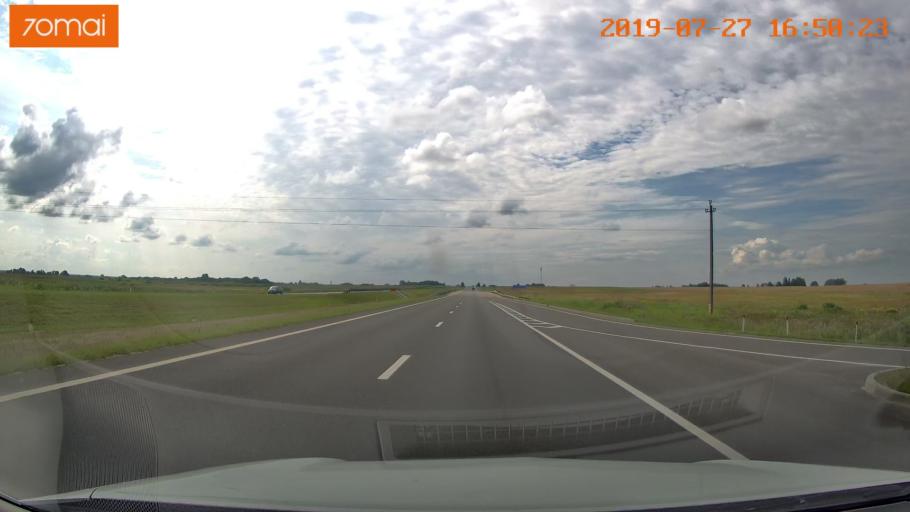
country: RU
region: Kaliningrad
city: Gvardeysk
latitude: 54.6773
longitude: 20.9150
